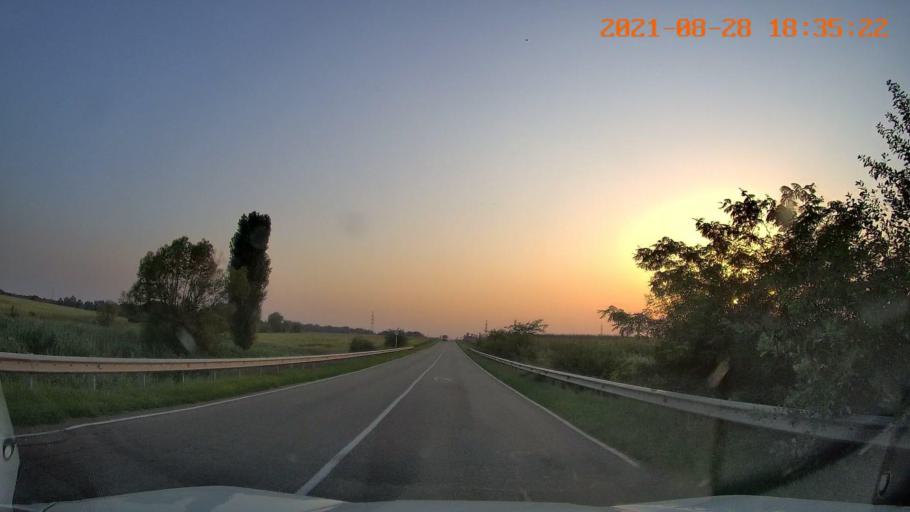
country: RU
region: Adygeya
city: Giaginskaya
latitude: 44.8734
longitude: 40.1350
